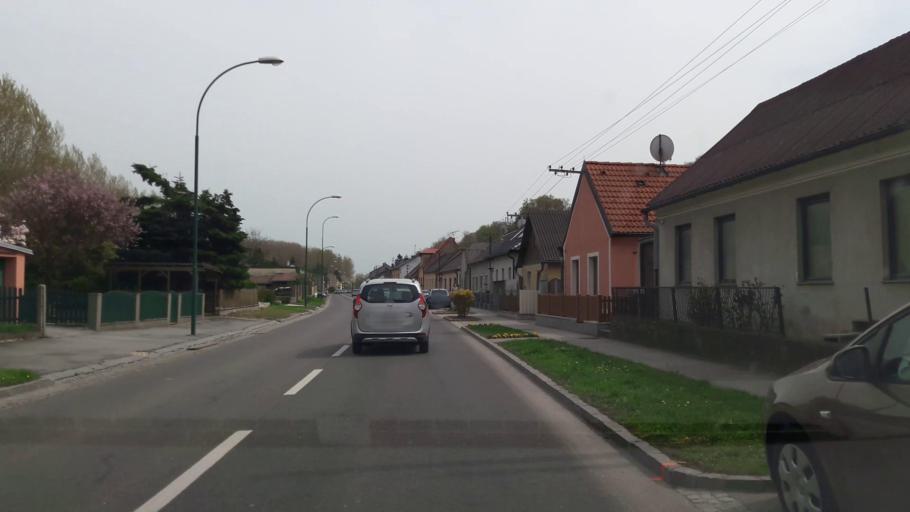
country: AT
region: Lower Austria
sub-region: Politischer Bezirk Bruck an der Leitha
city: Wolfsthal
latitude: 48.1329
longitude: 17.0166
